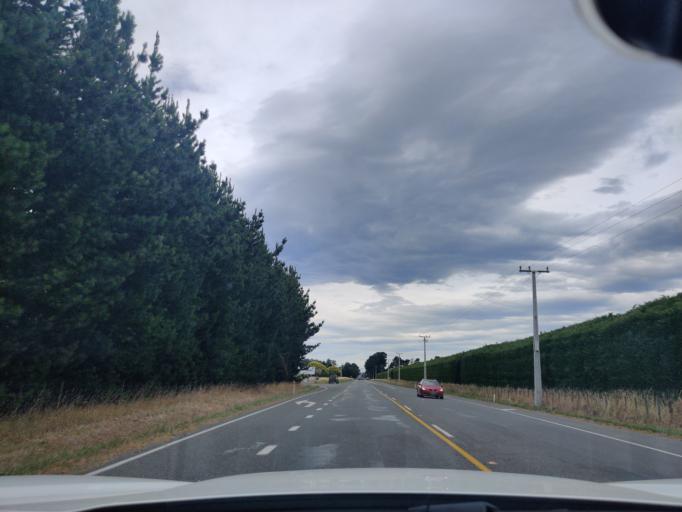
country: NZ
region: Wellington
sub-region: Masterton District
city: Masterton
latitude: -40.9890
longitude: 175.5732
